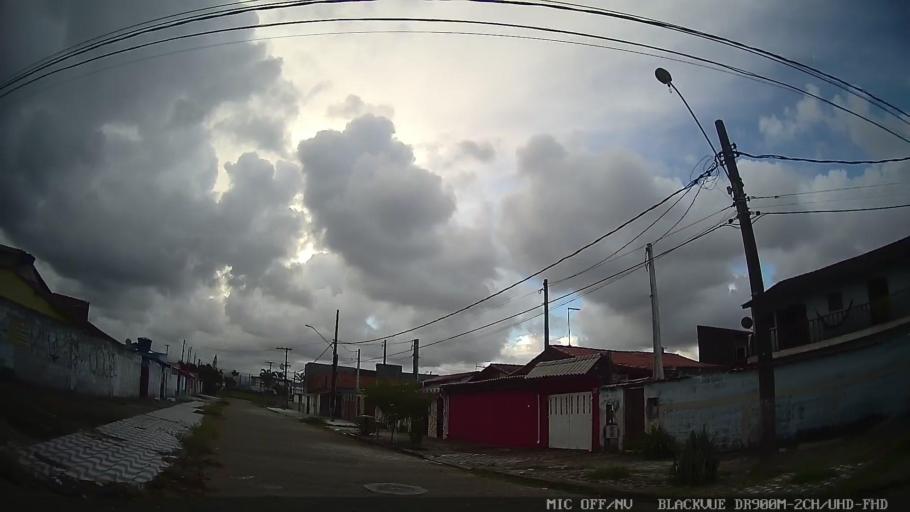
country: BR
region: Sao Paulo
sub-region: Itanhaem
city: Itanhaem
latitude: -24.1382
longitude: -46.7055
